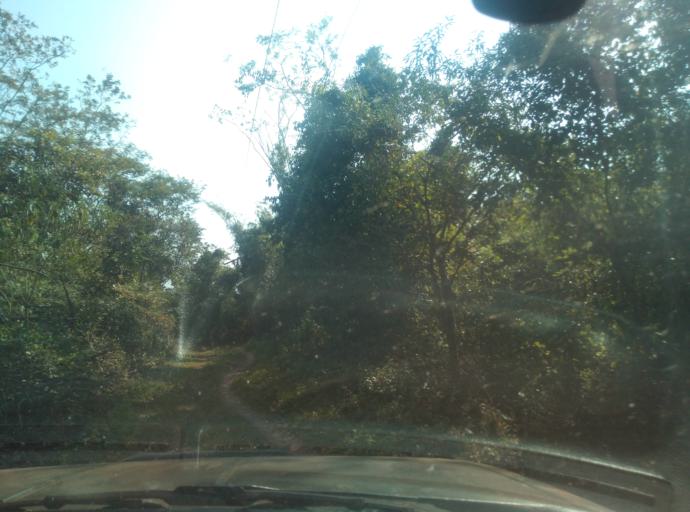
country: PY
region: Caaguazu
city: San Joaquin
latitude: -25.1567
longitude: -56.1255
